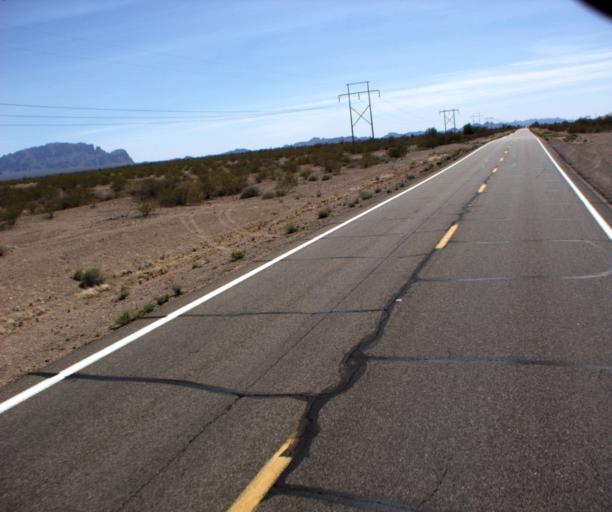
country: US
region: Arizona
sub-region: La Paz County
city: Quartzsite
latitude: 33.4837
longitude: -114.2170
